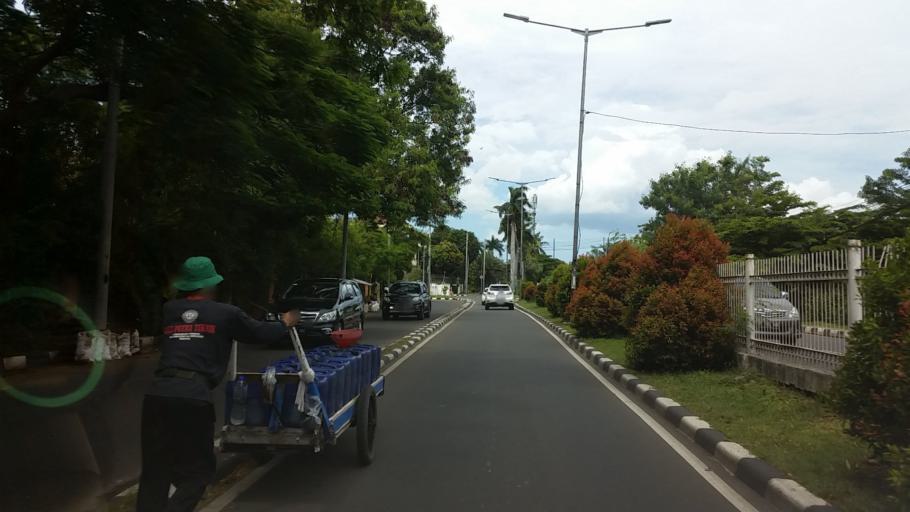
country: ID
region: Jakarta Raya
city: Jakarta
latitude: -6.1165
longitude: 106.7942
